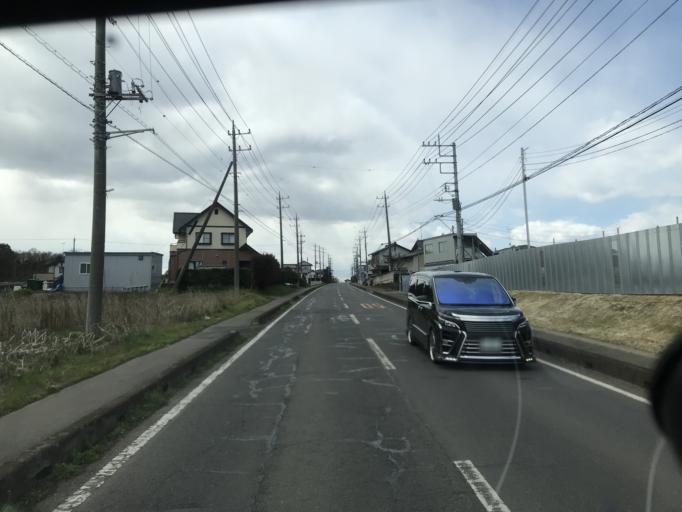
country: JP
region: Ibaraki
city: Shimodate
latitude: 36.2478
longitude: 139.9458
